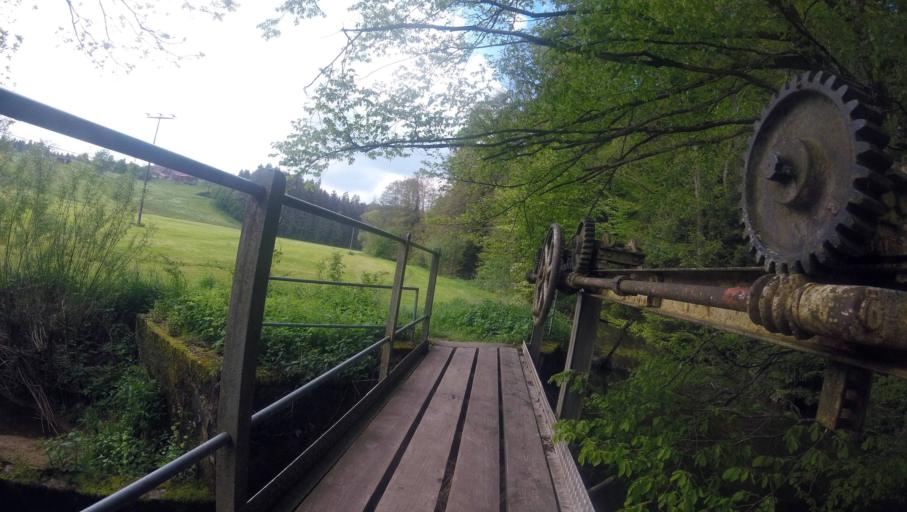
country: DE
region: Baden-Wuerttemberg
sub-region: Regierungsbezirk Stuttgart
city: Alfdorf
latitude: 48.8703
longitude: 9.7078
